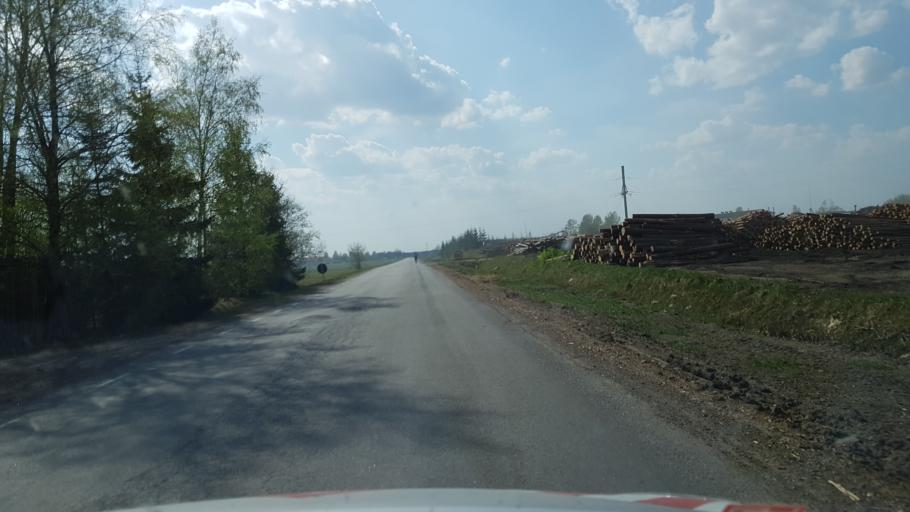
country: EE
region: Paernumaa
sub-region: Sauga vald
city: Sauga
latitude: 58.4380
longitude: 24.5320
